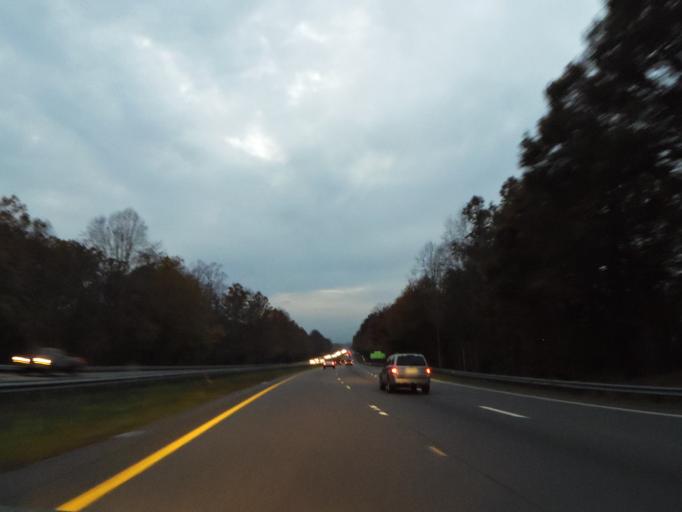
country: US
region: North Carolina
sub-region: McDowell County
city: West Marion
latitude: 35.6344
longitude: -82.0064
